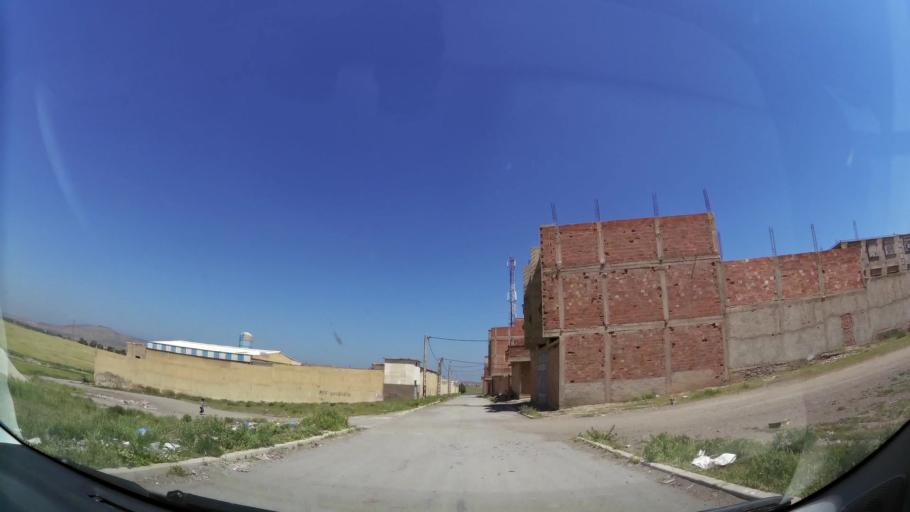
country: MA
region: Oriental
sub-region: Oujda-Angad
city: Oujda
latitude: 34.6820
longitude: -1.9604
